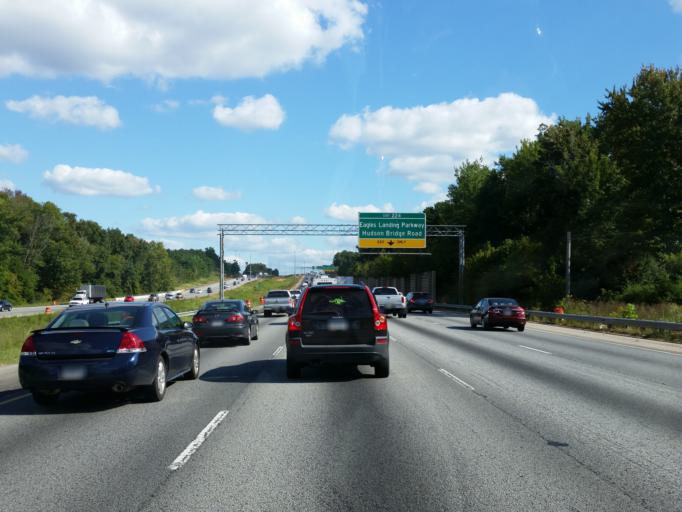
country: US
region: Georgia
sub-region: Henry County
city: Stockbridge
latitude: 33.5146
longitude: -84.2420
